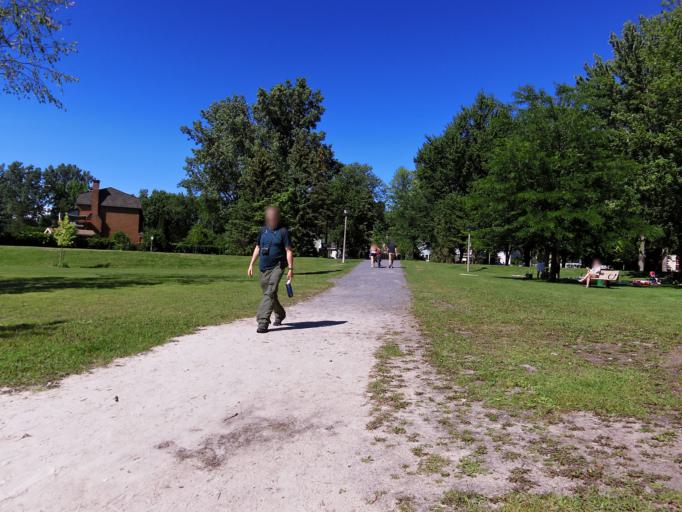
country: CA
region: Ontario
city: Bells Corners
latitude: 45.3655
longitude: -75.8005
